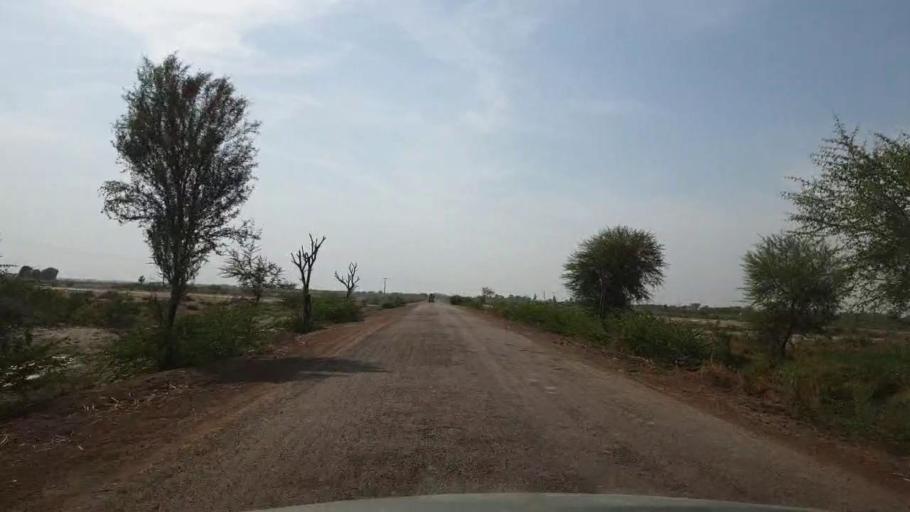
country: PK
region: Sindh
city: Kunri
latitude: 25.1570
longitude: 69.4847
